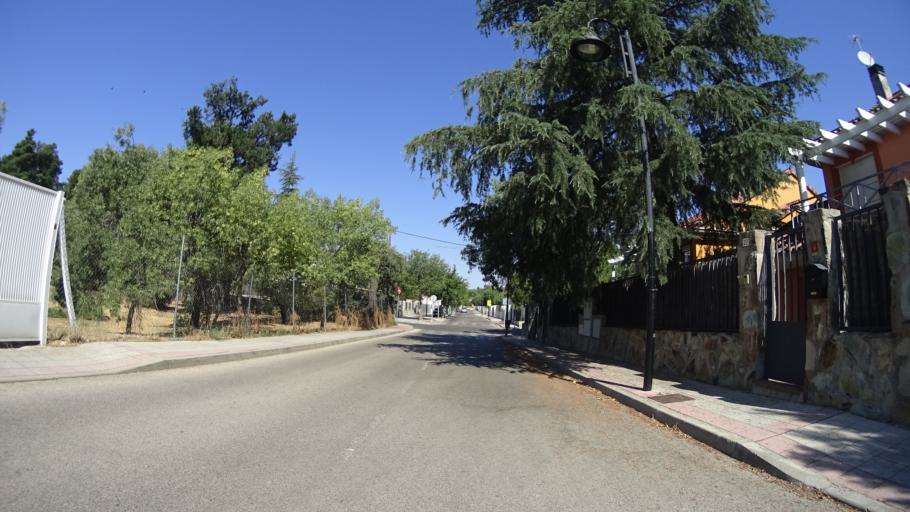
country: ES
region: Madrid
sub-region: Provincia de Madrid
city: Galapagar
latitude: 40.5951
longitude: -3.9827
